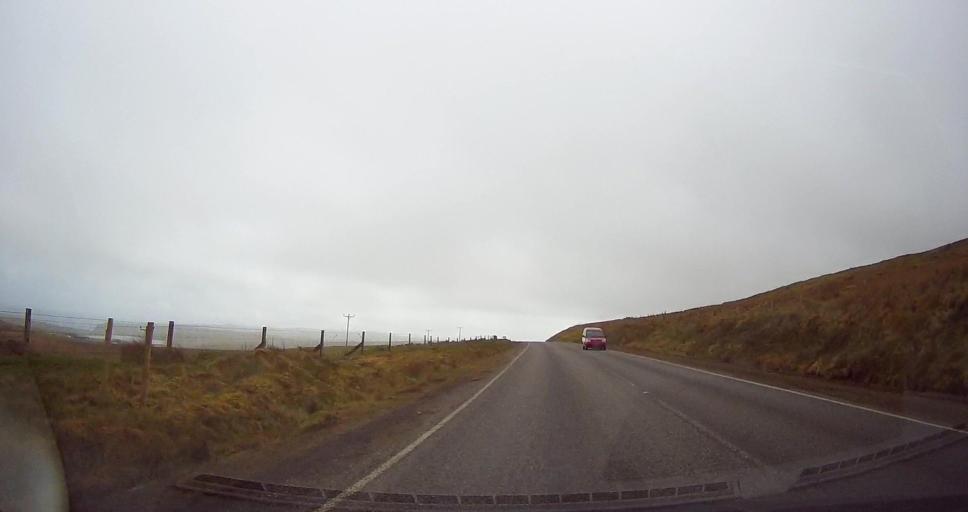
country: GB
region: Scotland
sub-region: Shetland Islands
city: Sandwick
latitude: 59.9586
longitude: -1.2854
